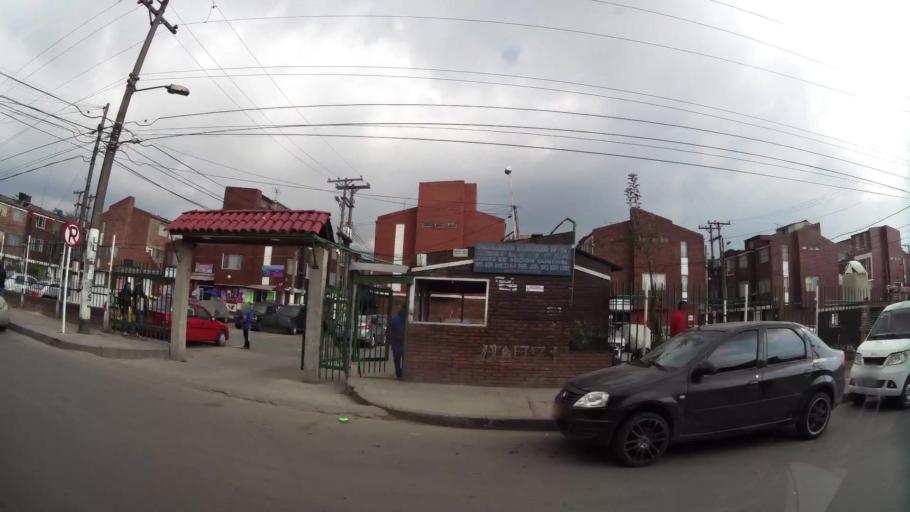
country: CO
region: Bogota D.C.
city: Bogota
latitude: 4.5539
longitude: -74.1136
